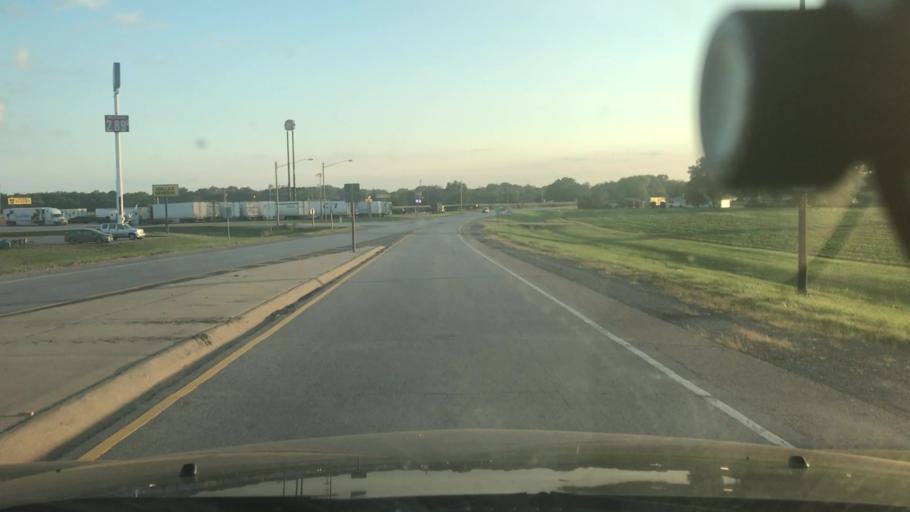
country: US
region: Illinois
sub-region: Washington County
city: Okawville
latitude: 38.4380
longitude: -89.5336
